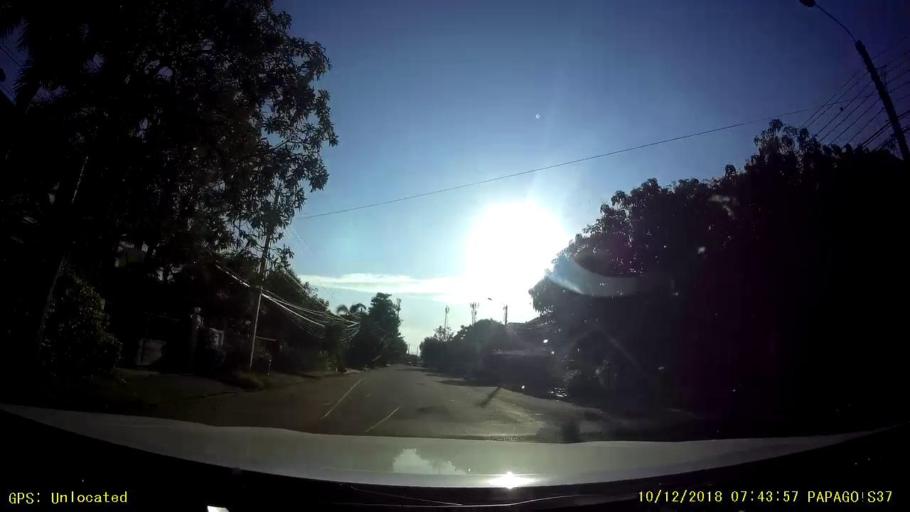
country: TH
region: Bangkok
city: Lat Krabang
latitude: 13.7911
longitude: 100.8165
